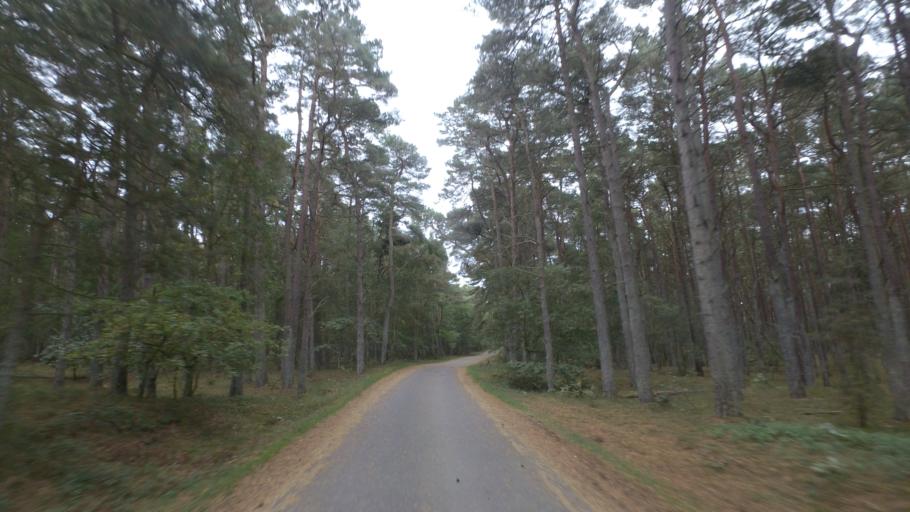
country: DK
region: Capital Region
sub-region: Bornholm Kommune
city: Nexo
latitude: 54.9994
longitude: 15.0391
